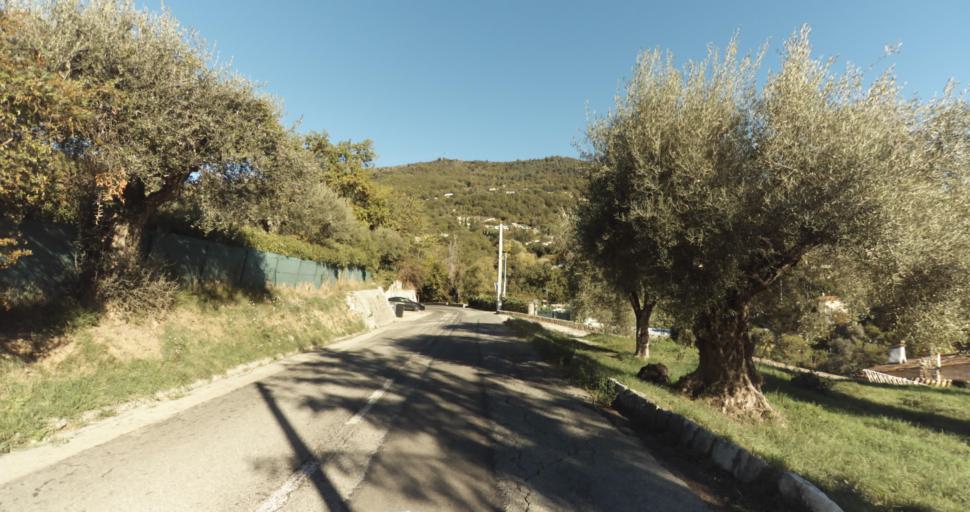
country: FR
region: Provence-Alpes-Cote d'Azur
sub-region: Departement des Alpes-Maritimes
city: Vence
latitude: 43.7257
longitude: 7.0871
